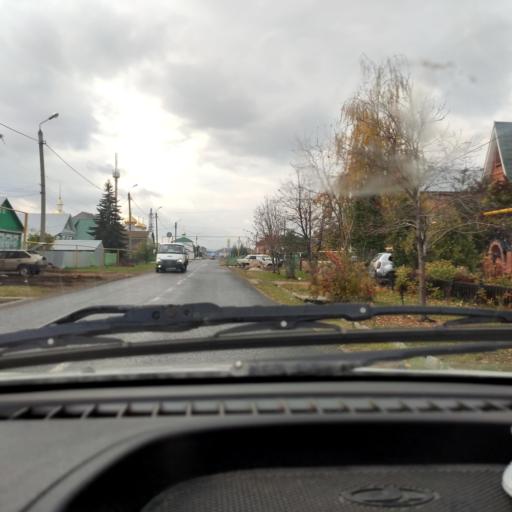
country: RU
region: Samara
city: Zhigulevsk
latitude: 53.4654
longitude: 49.6335
